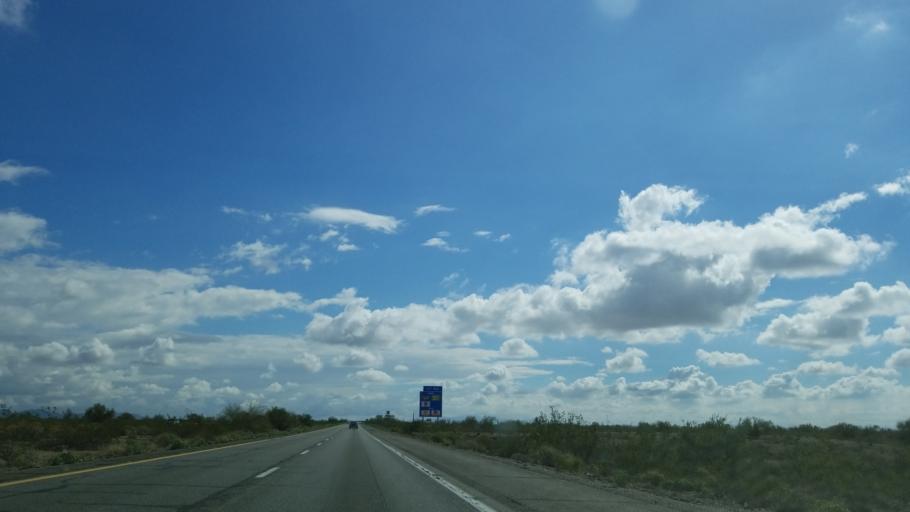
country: US
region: Arizona
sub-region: Maricopa County
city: Buckeye
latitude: 33.4665
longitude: -112.7996
